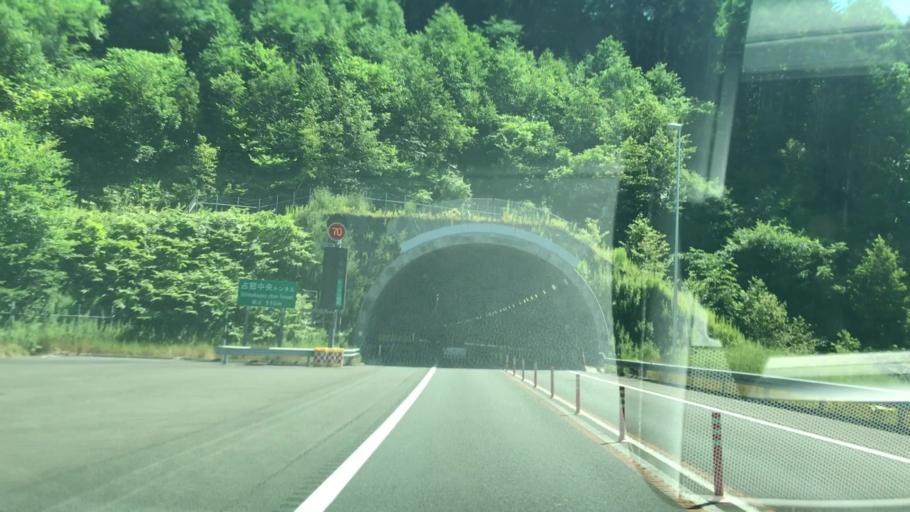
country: JP
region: Hokkaido
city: Shimo-furano
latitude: 42.9732
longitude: 142.3910
